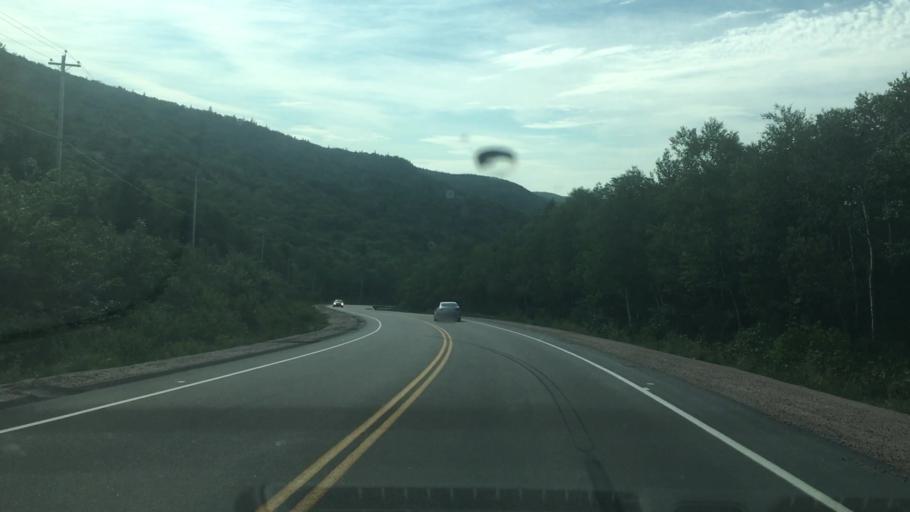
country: CA
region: Nova Scotia
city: Sydney Mines
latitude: 46.8555
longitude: -60.4498
